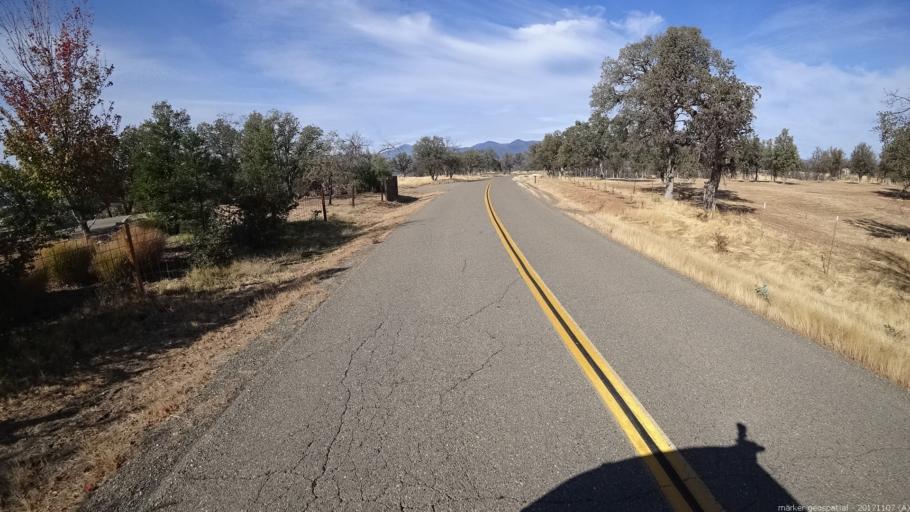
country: US
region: California
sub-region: Shasta County
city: Shasta
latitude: 40.4561
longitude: -122.5367
